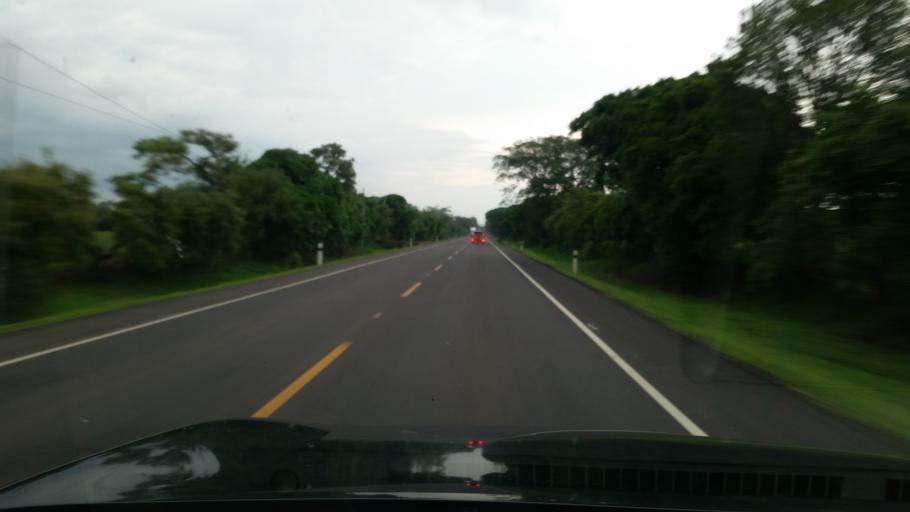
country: NI
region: Leon
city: Nagarote
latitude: 12.2920
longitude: -86.5890
